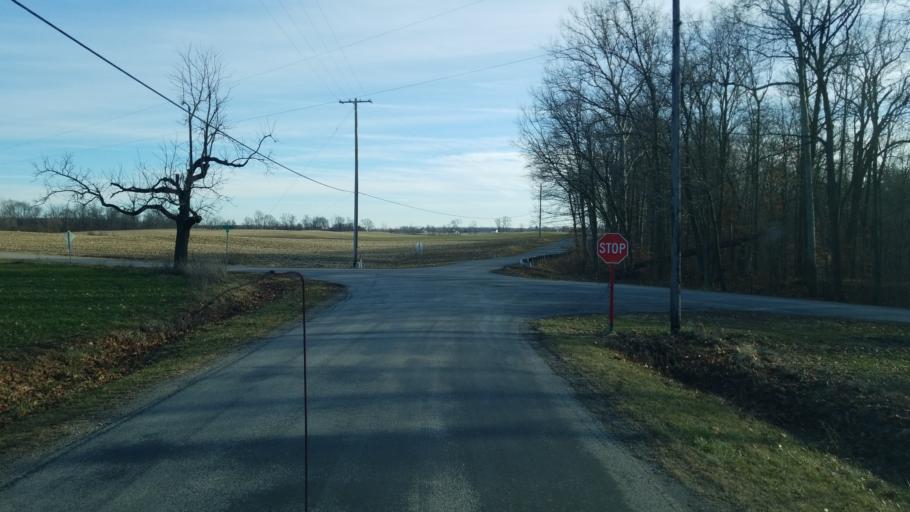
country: US
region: Ohio
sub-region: Huron County
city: Monroeville
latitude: 41.1758
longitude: -82.6964
